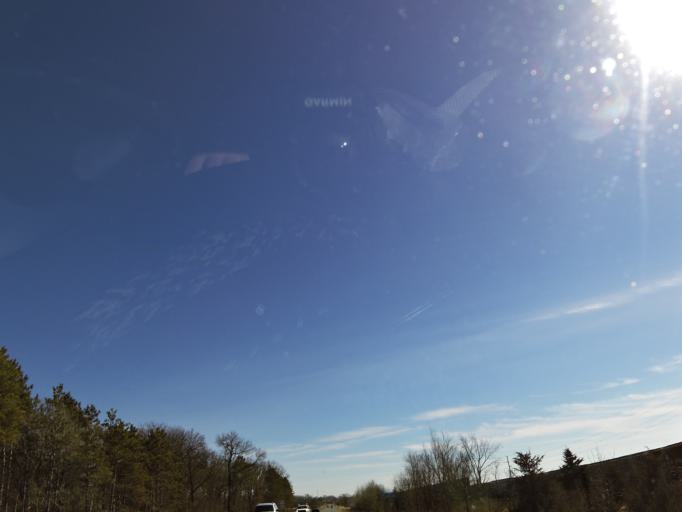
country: US
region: Minnesota
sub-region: Wright County
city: Buffalo
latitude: 45.1271
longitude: -93.8181
